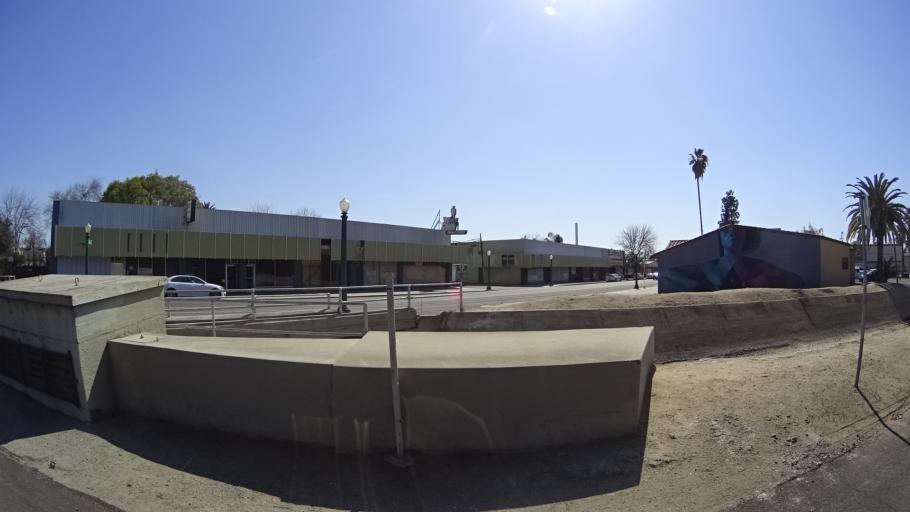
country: US
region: California
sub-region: Fresno County
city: Fresno
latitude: 36.7534
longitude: -119.8006
